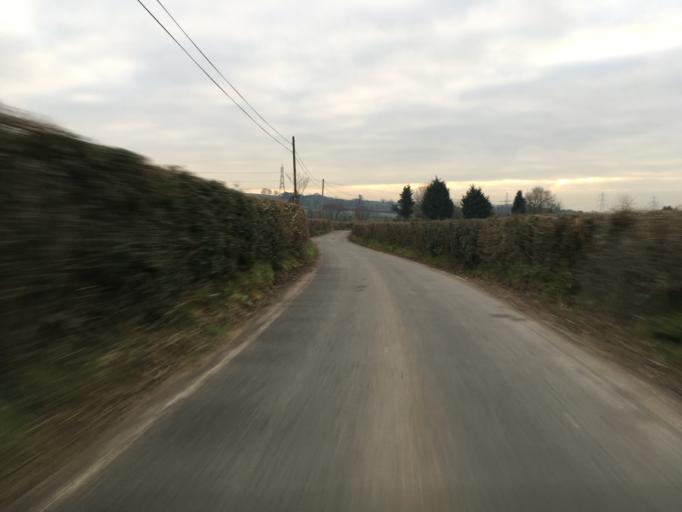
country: GB
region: Wales
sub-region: Newport
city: Marshfield
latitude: 51.5683
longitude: -3.0797
